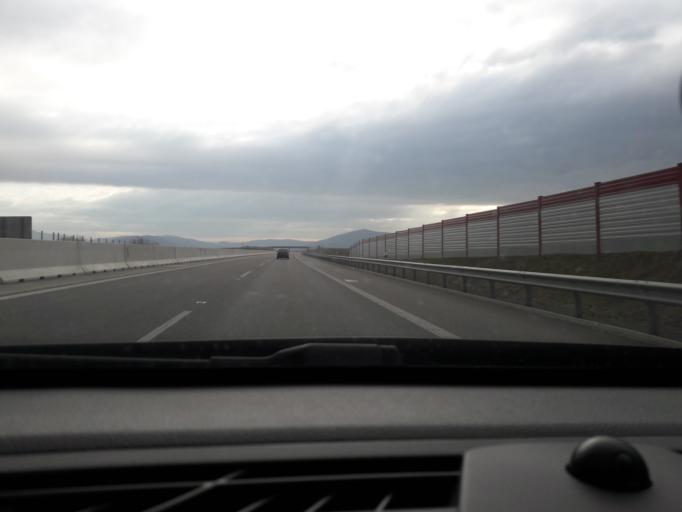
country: SK
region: Banskobystricky
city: Hrochot,Slovakia
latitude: 48.5720
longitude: 19.2664
